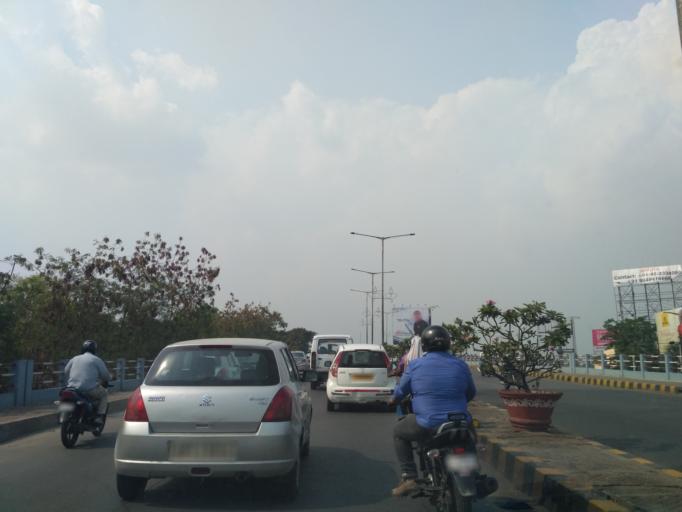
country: IN
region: Telangana
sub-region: Hyderabad
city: Hyderabad
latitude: 17.4141
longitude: 78.4608
